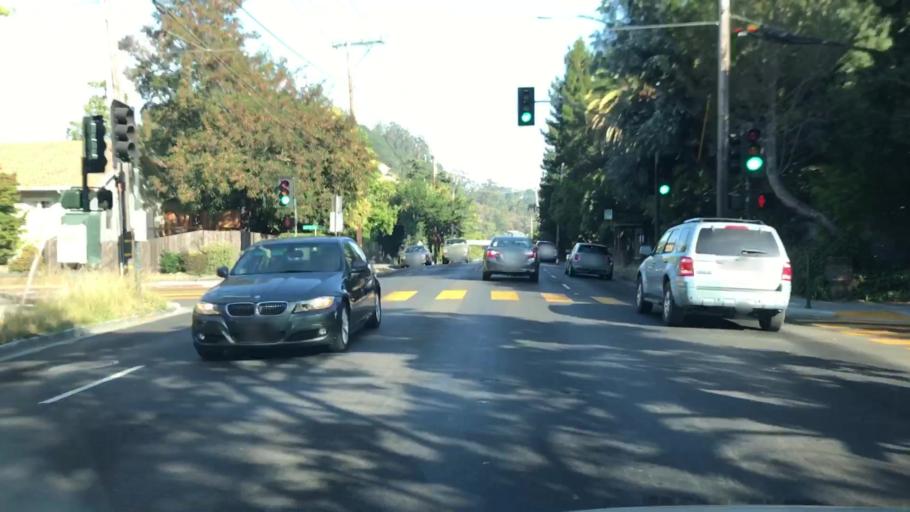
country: US
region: California
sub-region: Marin County
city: San Anselmo
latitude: 37.9825
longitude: -122.5692
